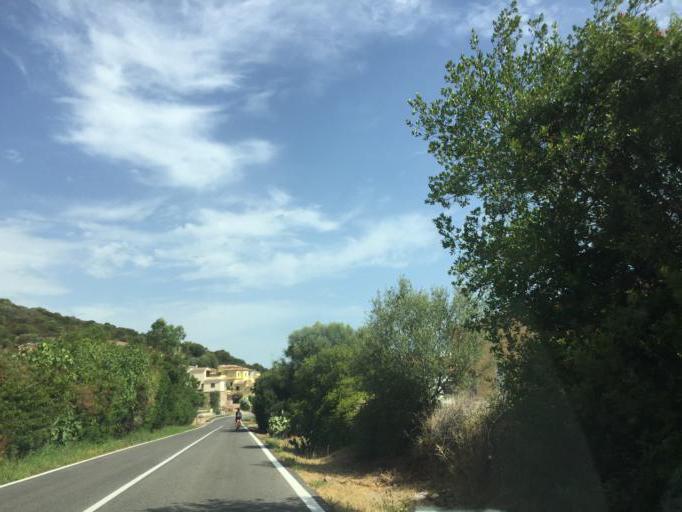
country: IT
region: Sardinia
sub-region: Provincia di Olbia-Tempio
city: San Teodoro
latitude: 40.7386
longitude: 9.6467
